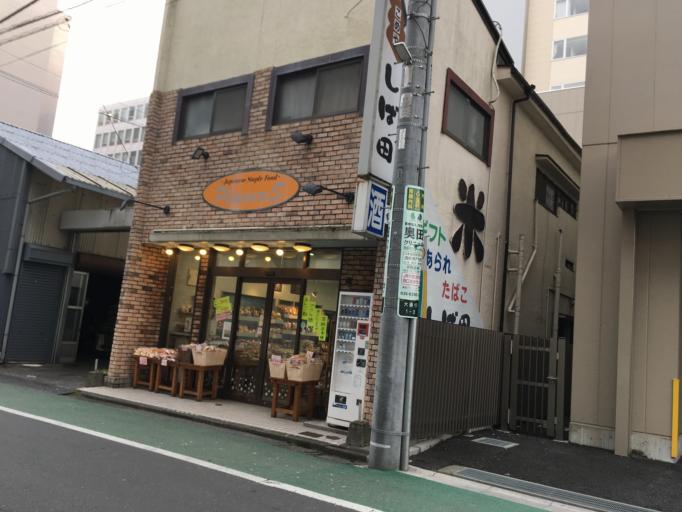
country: JP
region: Tochigi
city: Utsunomiya-shi
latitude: 36.5611
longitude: 139.8916
